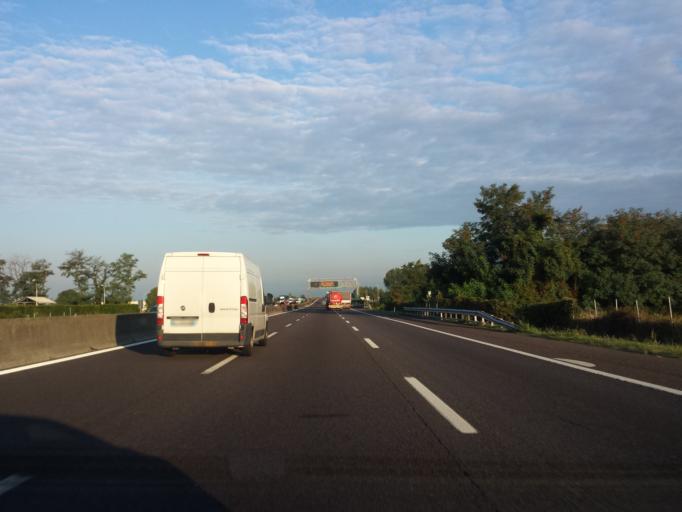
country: IT
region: Lombardy
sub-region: Provincia di Bergamo
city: Grumello del Monte
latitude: 45.6293
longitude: 9.8728
